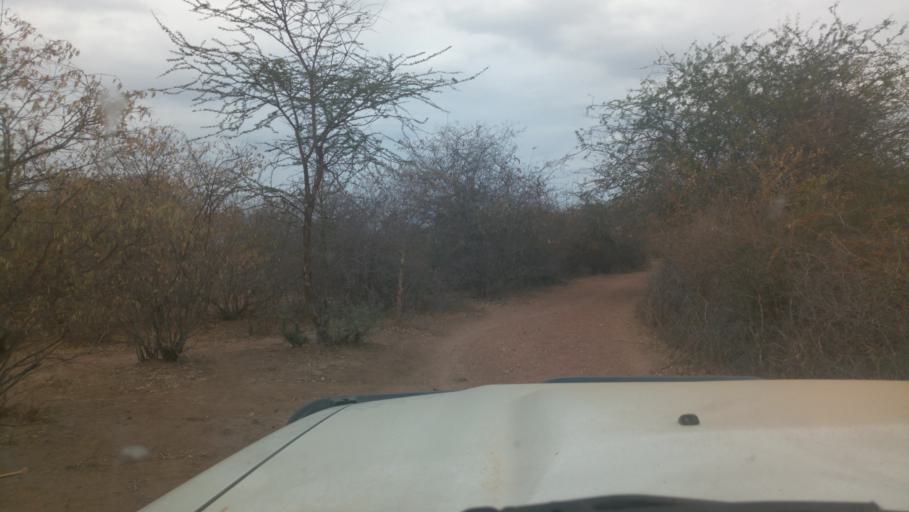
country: KE
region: Kitui
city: Kitui
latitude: -1.6178
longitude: 37.9235
